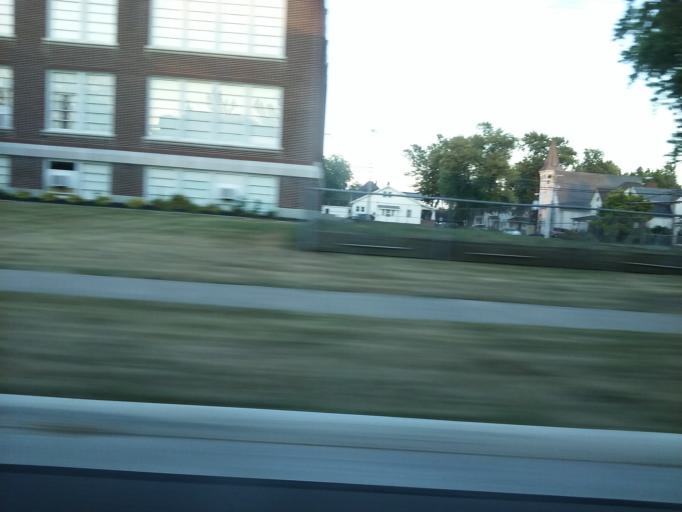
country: US
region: Ohio
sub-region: Hancock County
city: Findlay
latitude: 41.0490
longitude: -83.6500
